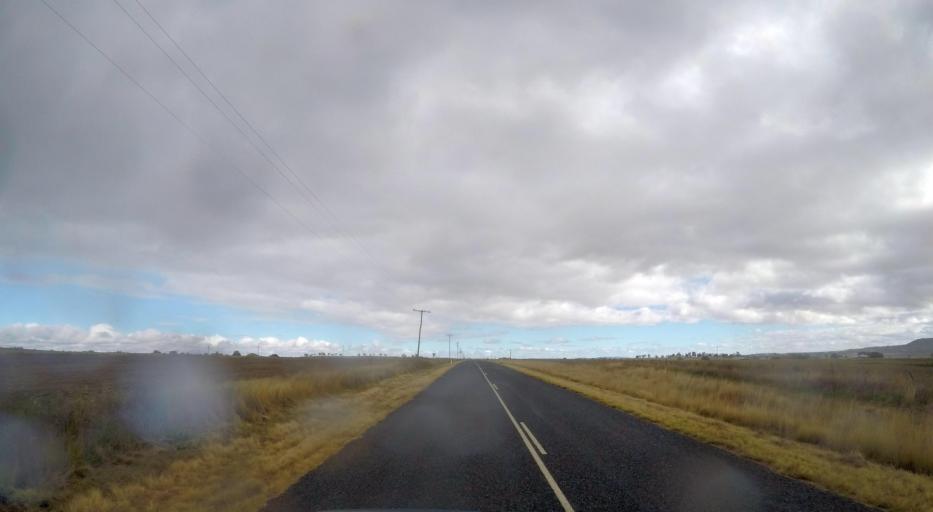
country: AU
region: Queensland
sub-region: Southern Downs
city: Warwick
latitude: -28.0528
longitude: 152.0296
